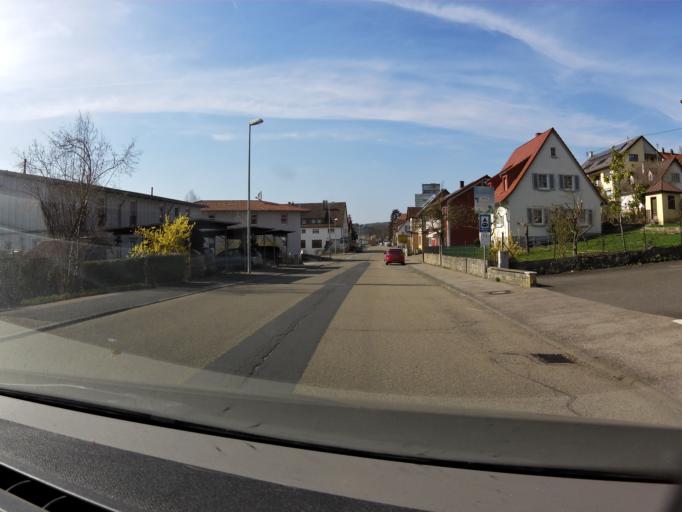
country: DE
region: Baden-Wuerttemberg
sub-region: Regierungsbezirk Stuttgart
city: Creglingen
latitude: 49.4694
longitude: 10.0350
